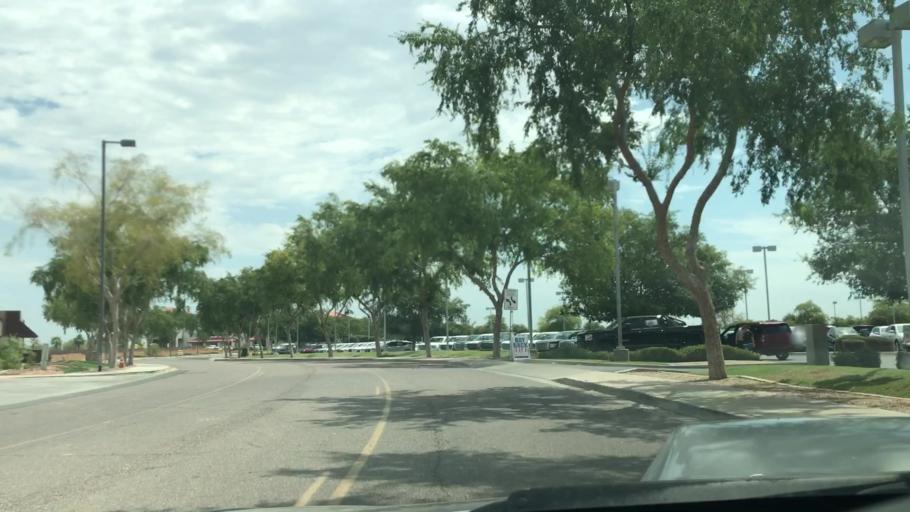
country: US
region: Arizona
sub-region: Maricopa County
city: Goodyear
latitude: 33.4553
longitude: -112.3571
